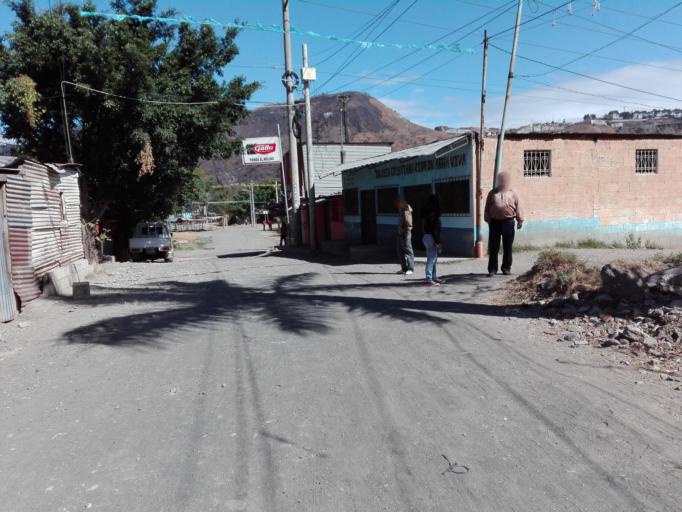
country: GT
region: Guatemala
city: Amatitlan
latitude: 14.4755
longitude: -90.5981
